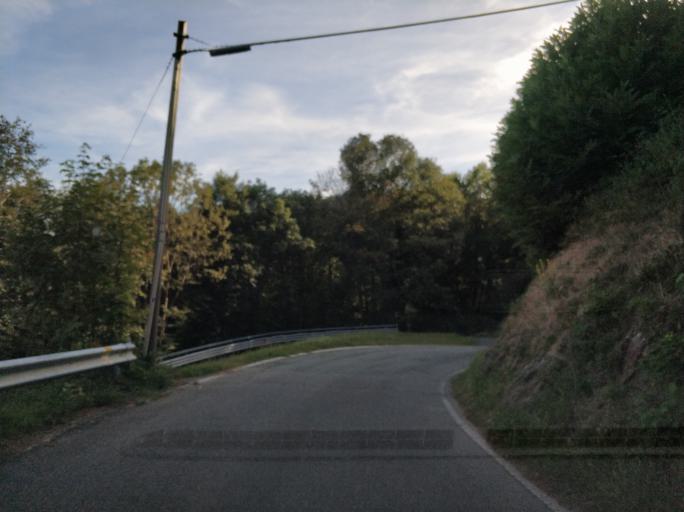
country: IT
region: Piedmont
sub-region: Provincia di Torino
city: Monastero di Lanzo
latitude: 45.3018
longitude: 7.4290
